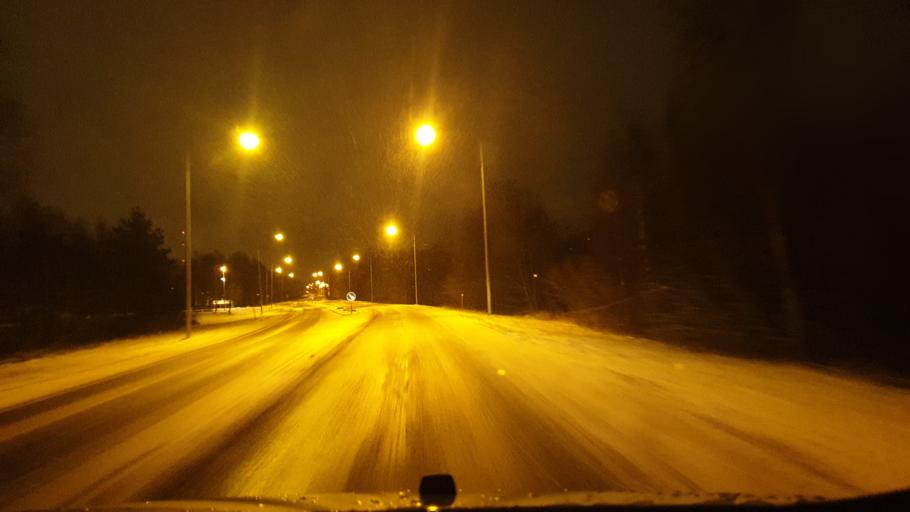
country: FI
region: Northern Ostrobothnia
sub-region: Oulu
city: Oulu
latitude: 64.9831
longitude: 25.4534
